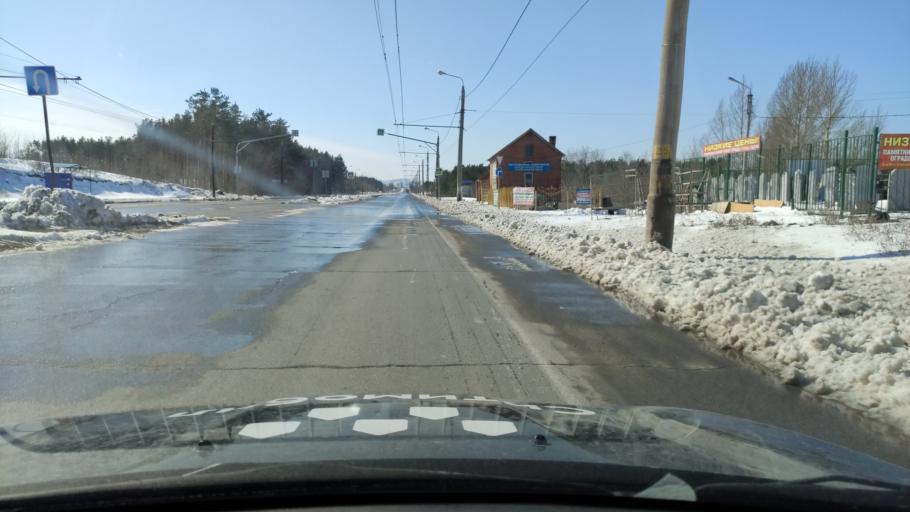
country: RU
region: Samara
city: Zhigulevsk
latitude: 53.5283
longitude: 49.5504
